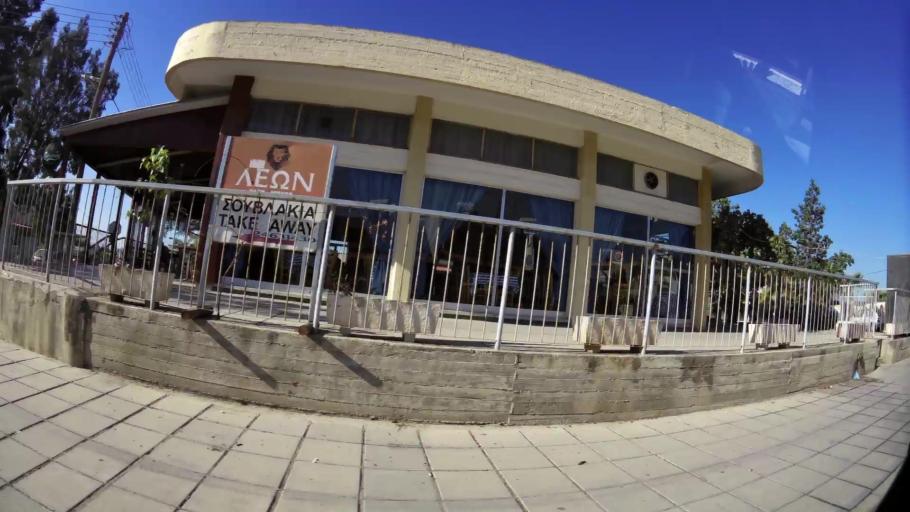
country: CY
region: Larnaka
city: Larnaca
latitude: 34.9347
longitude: 33.6118
